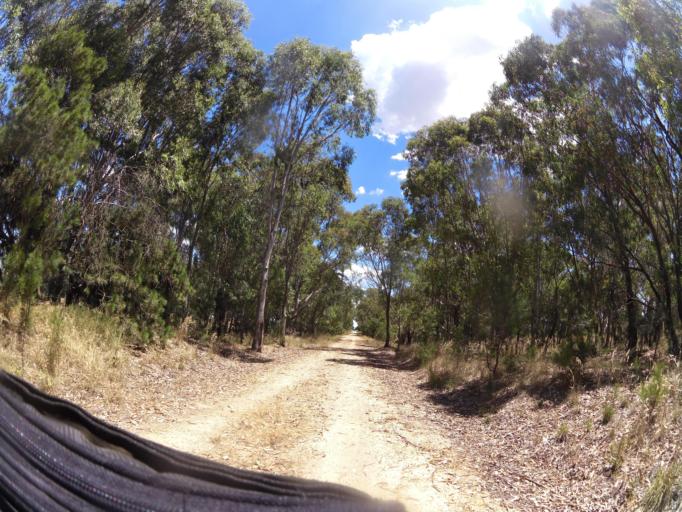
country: AU
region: Victoria
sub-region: Wellington
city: Heyfield
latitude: -37.9816
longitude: 146.8357
